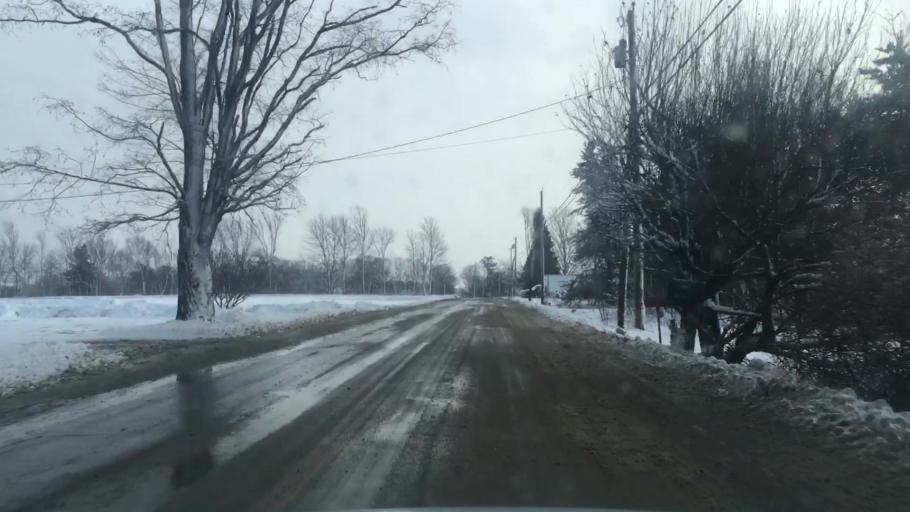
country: US
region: Maine
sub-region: Waldo County
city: Palermo
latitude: 44.3571
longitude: -69.4529
